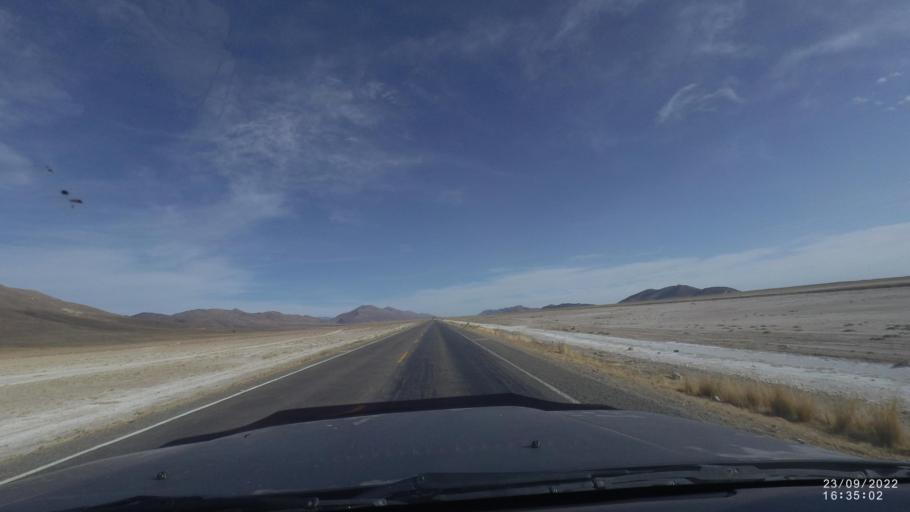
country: BO
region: Oruro
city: Machacamarca
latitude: -18.1982
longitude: -67.0125
